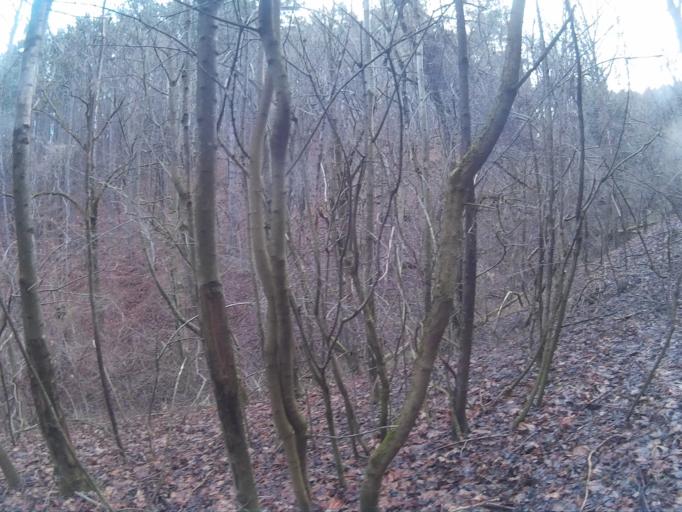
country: HU
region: Veszprem
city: Urkut
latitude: 47.1344
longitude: 17.6457
